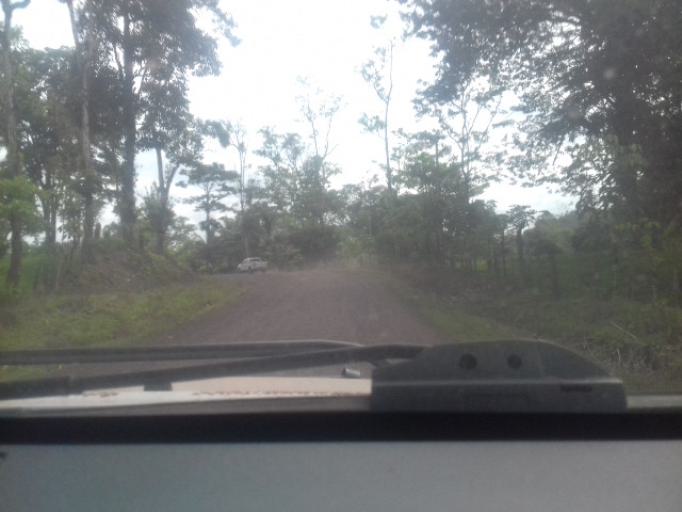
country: NI
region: Atlantico Norte (RAAN)
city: Waslala
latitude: 13.4133
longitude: -85.3200
